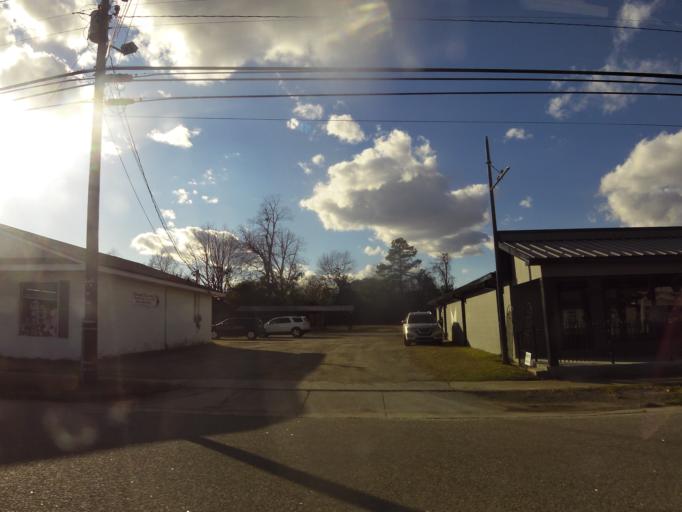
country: US
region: South Carolina
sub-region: Clarendon County
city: Manning
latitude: 33.6922
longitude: -80.2121
